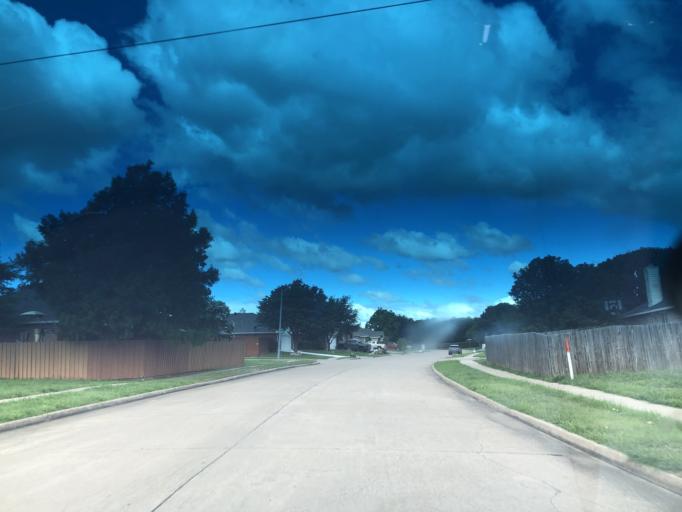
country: US
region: Texas
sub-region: Dallas County
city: Grand Prairie
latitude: 32.6959
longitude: -97.0344
